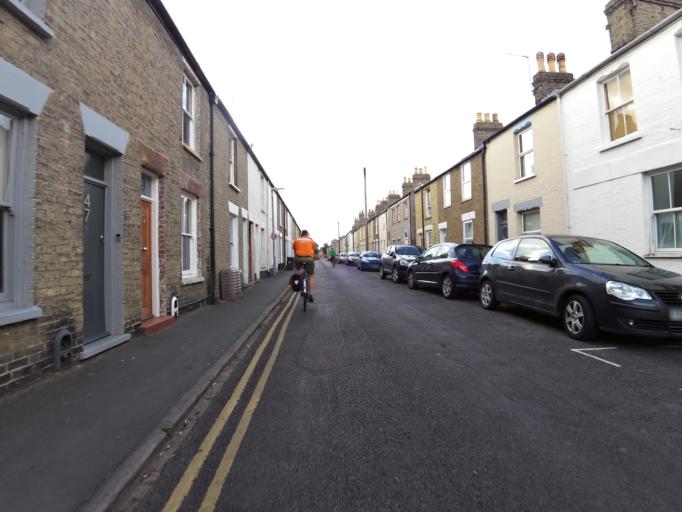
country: GB
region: England
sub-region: Cambridgeshire
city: Cambridge
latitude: 52.2046
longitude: 0.1419
